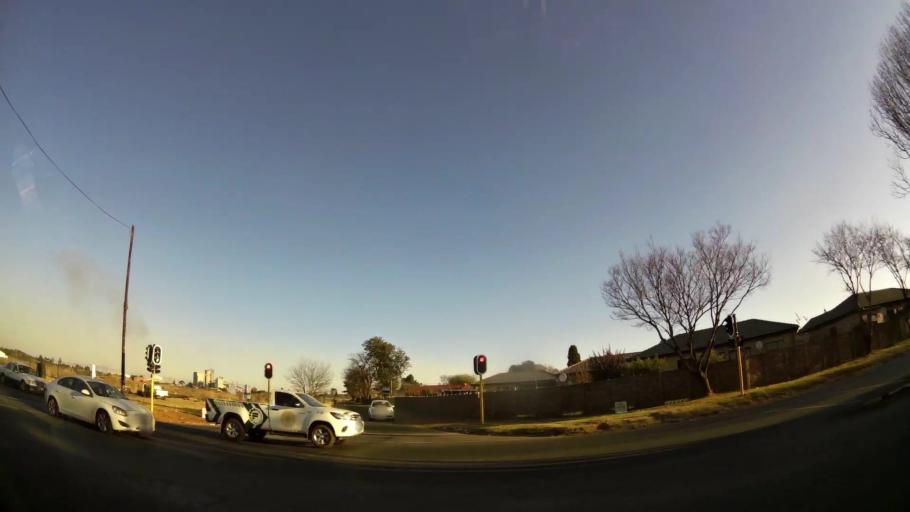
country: ZA
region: Gauteng
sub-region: City of Johannesburg Metropolitan Municipality
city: Roodepoort
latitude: -26.1703
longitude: 27.8835
